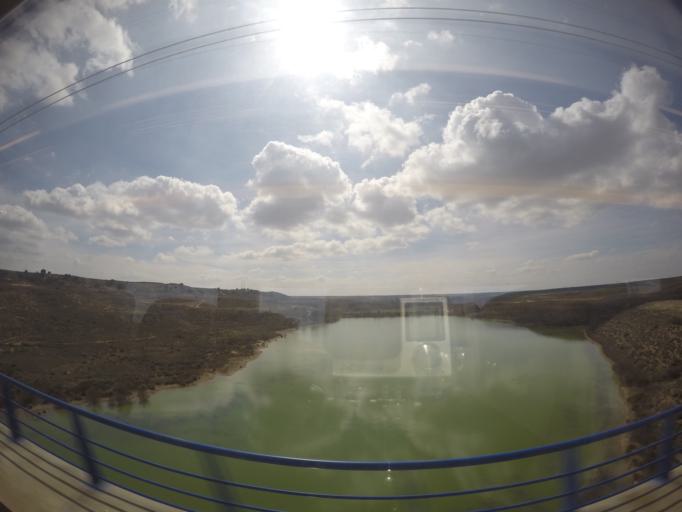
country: ES
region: Aragon
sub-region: Provincia de Huesca
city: Candasnos
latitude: 41.5451
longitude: 0.0608
